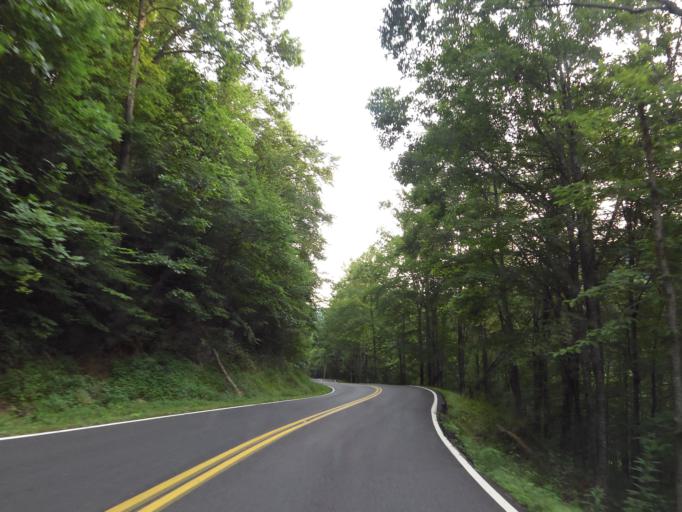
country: US
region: Tennessee
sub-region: Anderson County
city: Clinton
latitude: 36.1254
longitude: -84.2336
